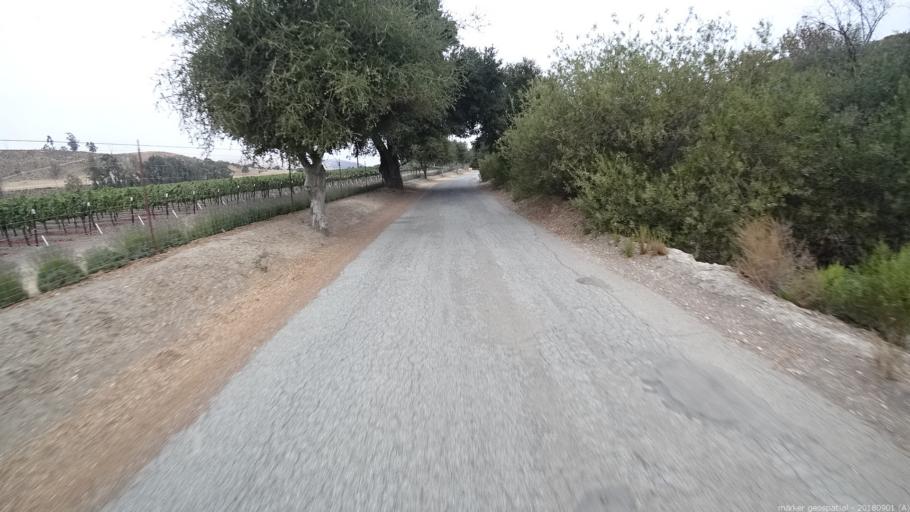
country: US
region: California
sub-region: Monterey County
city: Greenfield
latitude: 36.2754
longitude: -121.3021
